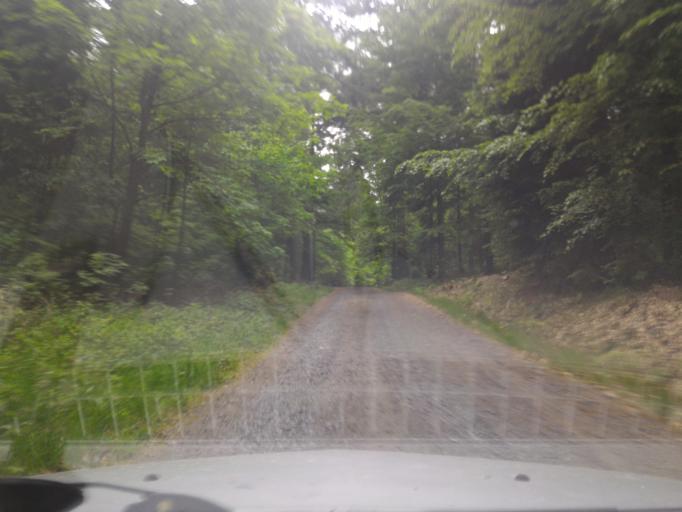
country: DE
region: Saxony
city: Kurort Jonsdorf
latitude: 50.8527
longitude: 14.6859
